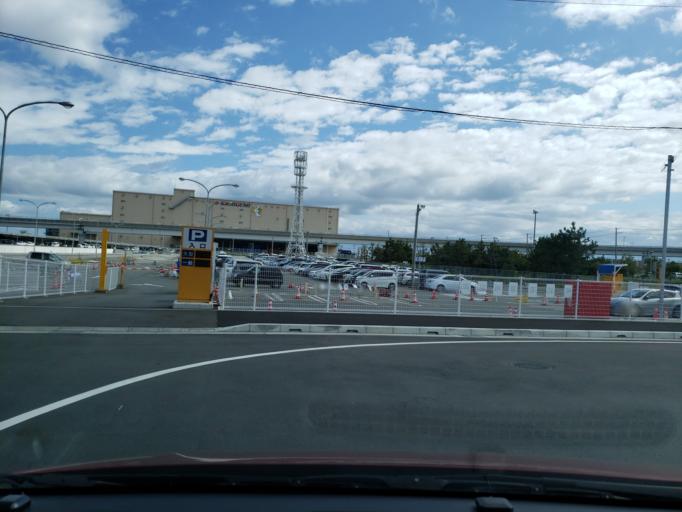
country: JP
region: Hyogo
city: Kobe
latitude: 34.6397
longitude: 135.2301
